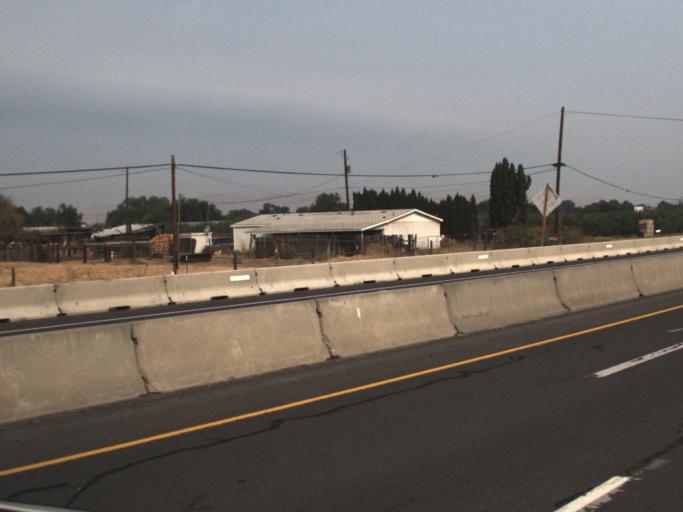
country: US
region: Washington
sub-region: Yakima County
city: Wapato
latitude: 46.4542
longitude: -120.4301
